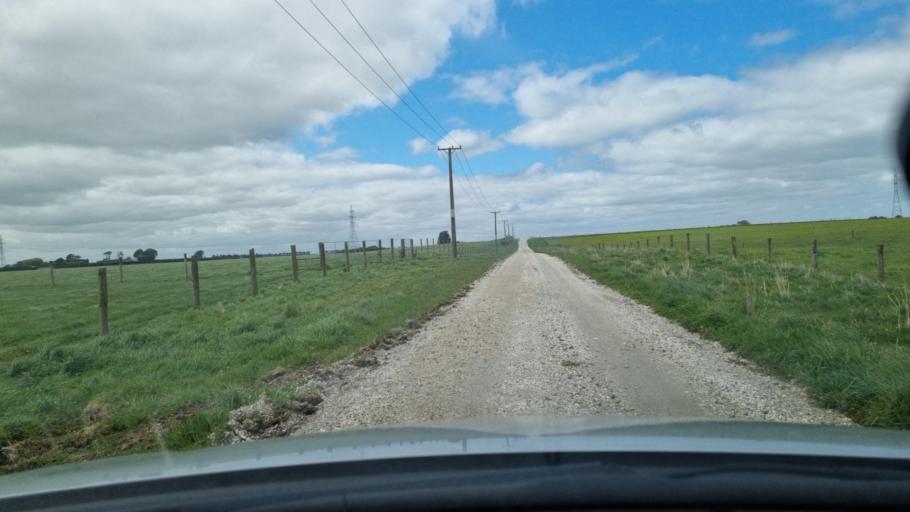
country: NZ
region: Southland
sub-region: Invercargill City
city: Invercargill
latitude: -46.4427
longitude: 168.4444
